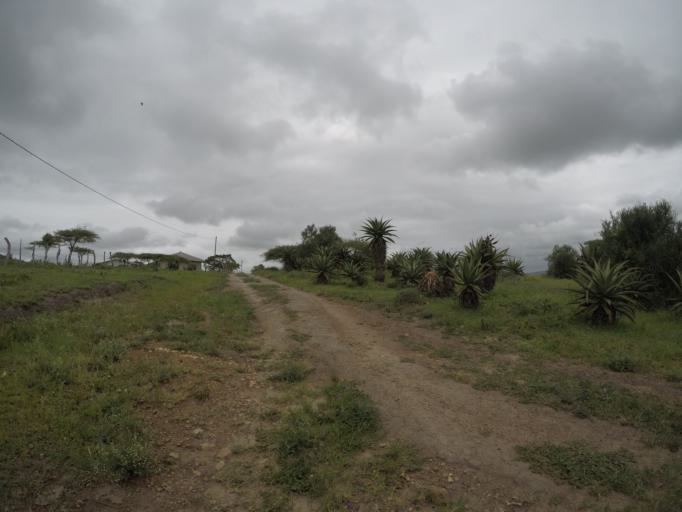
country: ZA
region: KwaZulu-Natal
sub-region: uThungulu District Municipality
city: Empangeni
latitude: -28.5959
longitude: 31.8507
